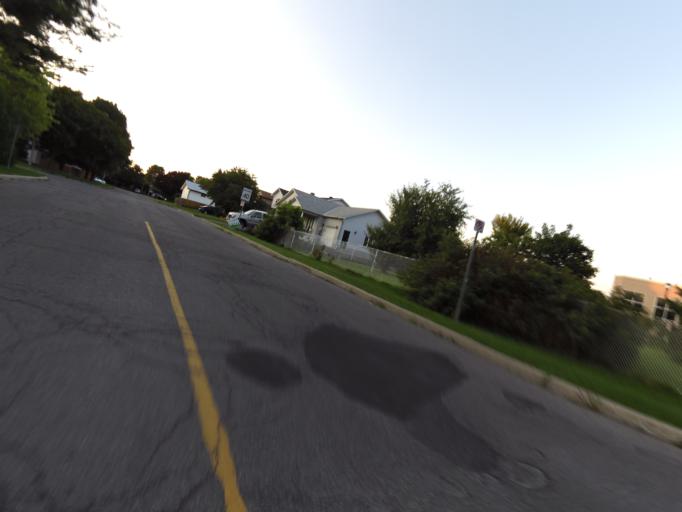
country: CA
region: Quebec
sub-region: Outaouais
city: Gatineau
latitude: 45.4676
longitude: -75.4929
